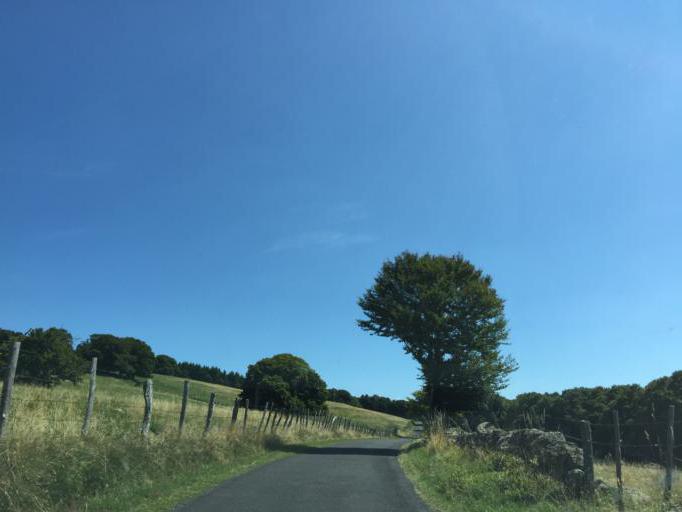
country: FR
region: Midi-Pyrenees
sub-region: Departement de l'Aveyron
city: Laguiole
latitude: 44.6535
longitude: 2.9168
